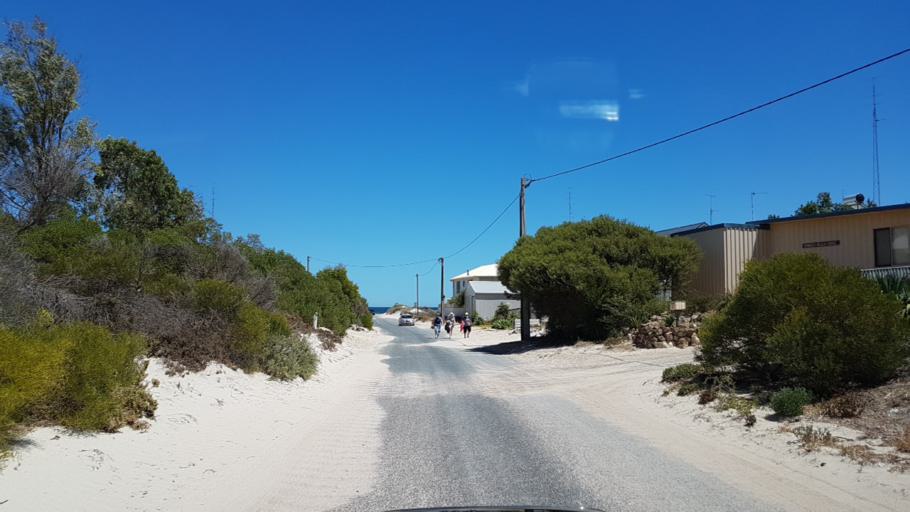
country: AU
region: South Australia
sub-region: Copper Coast
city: Wallaroo
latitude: -33.9068
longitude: 137.6329
